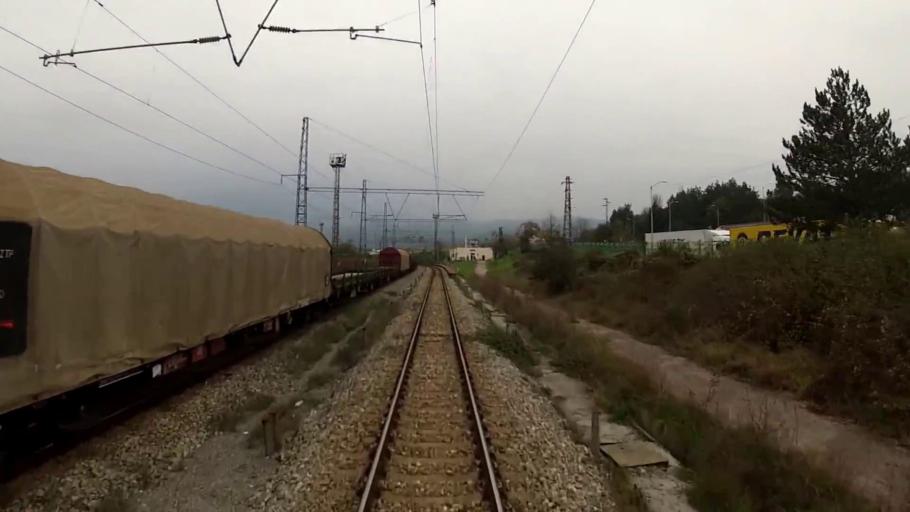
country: RS
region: Central Serbia
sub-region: Pirotski Okrug
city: Dimitrovgrad
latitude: 42.9976
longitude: 22.8370
